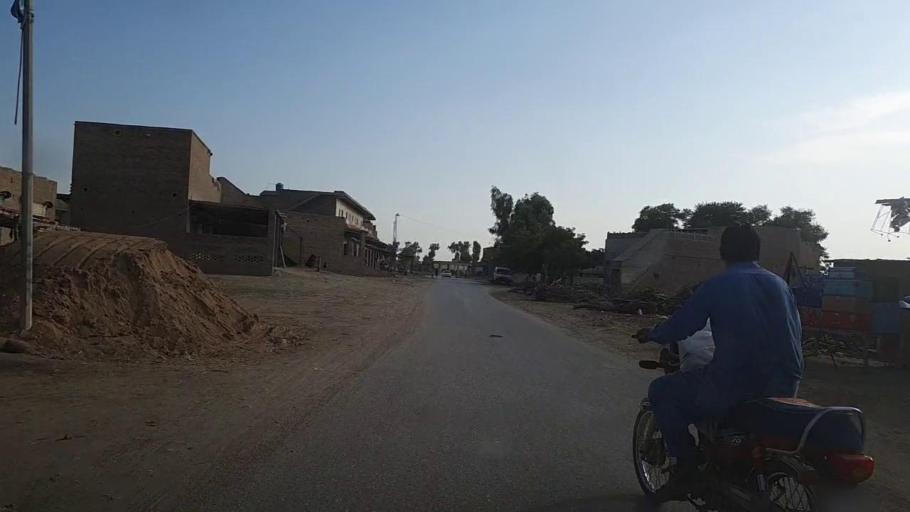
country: PK
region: Sindh
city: Thul
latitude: 28.1787
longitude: 68.7243
